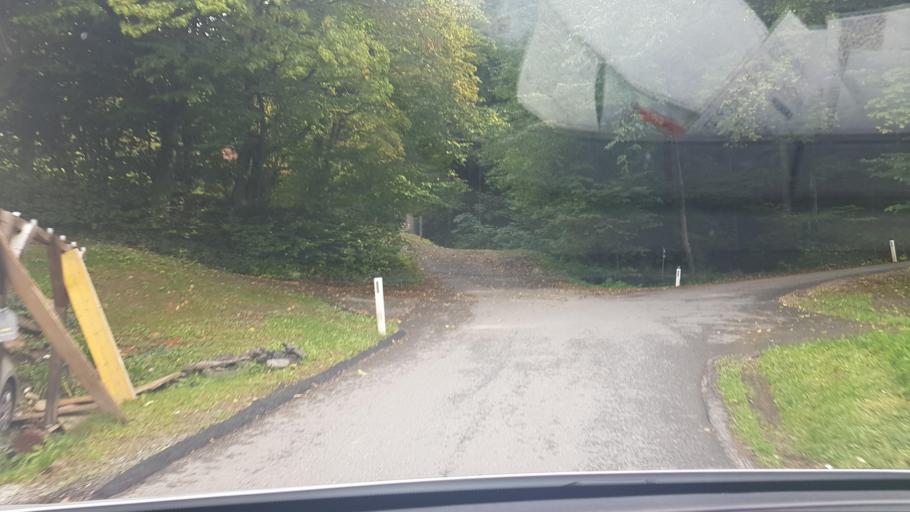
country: AT
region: Styria
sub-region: Politischer Bezirk Leibnitz
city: Sankt Johann im Saggautal
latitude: 46.7179
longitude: 15.4240
